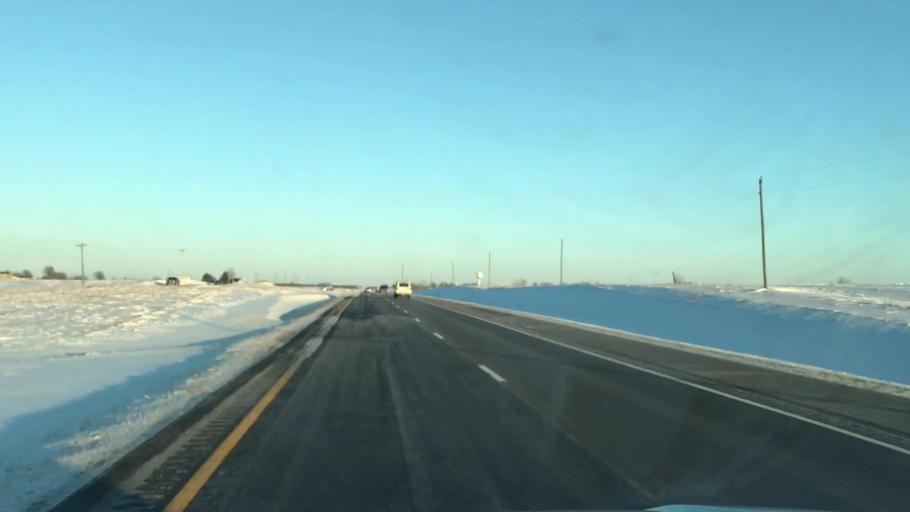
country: US
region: Missouri
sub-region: Clinton County
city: Gower
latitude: 39.7620
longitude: -94.5242
